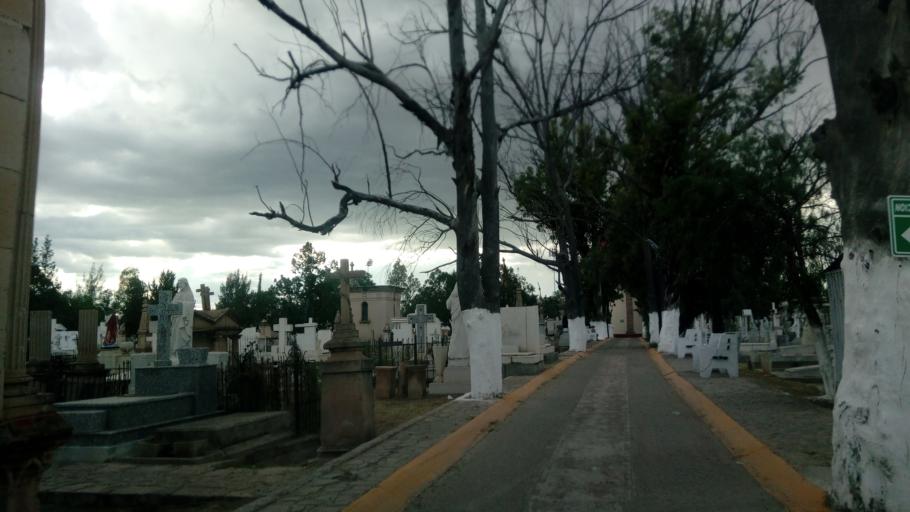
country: MX
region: Durango
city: Victoria de Durango
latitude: 24.0279
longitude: -104.6404
